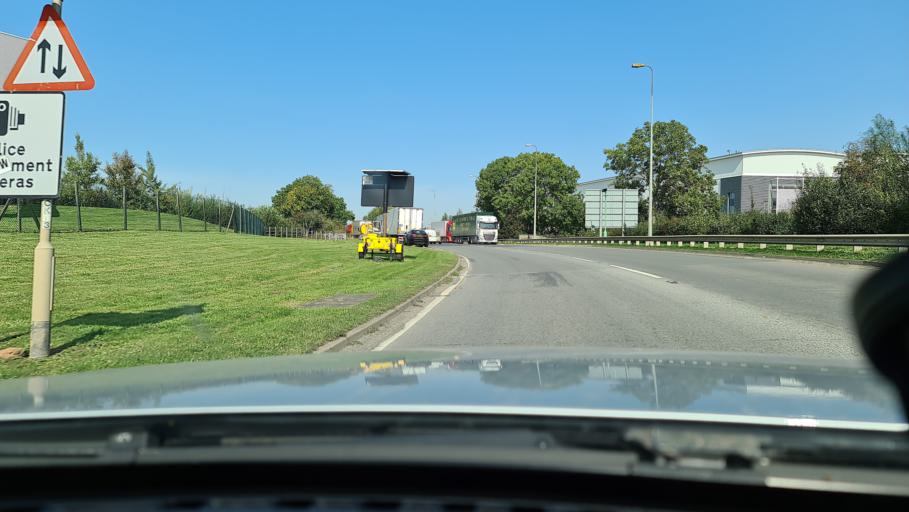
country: GB
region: England
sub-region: Warwickshire
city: Rugby
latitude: 52.3588
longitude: -1.1701
